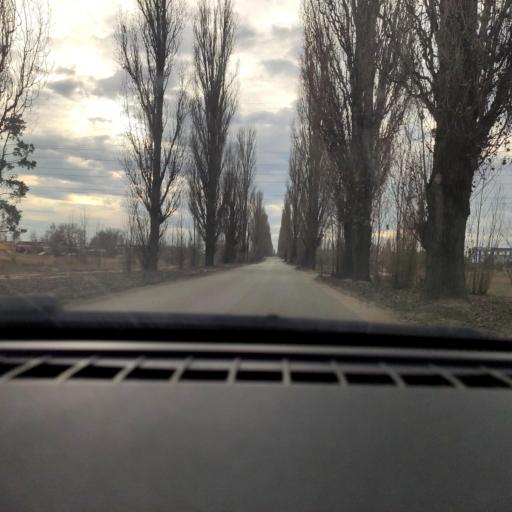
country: RU
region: Voronezj
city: Maslovka
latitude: 51.6050
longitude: 39.2206
